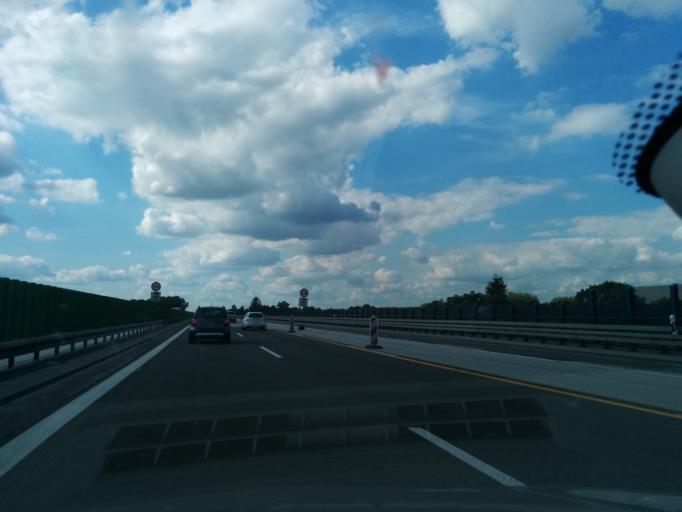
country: DE
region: Brandenburg
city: Woltersdorf
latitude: 52.4717
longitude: 13.7720
